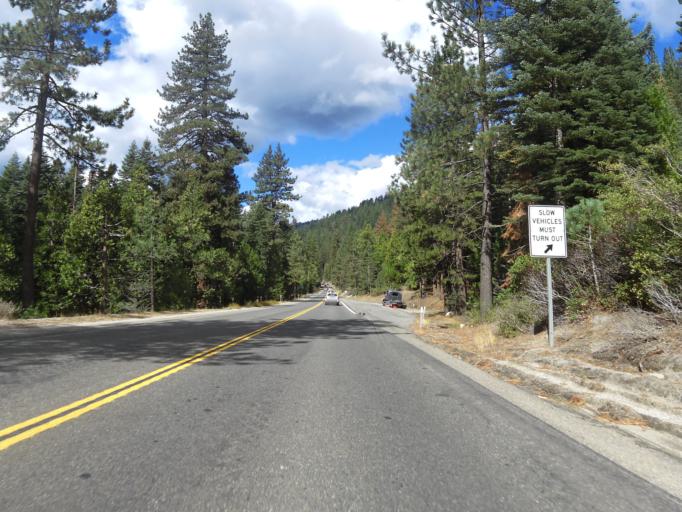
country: US
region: California
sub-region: El Dorado County
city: South Lake Tahoe
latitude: 38.7871
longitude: -120.1600
